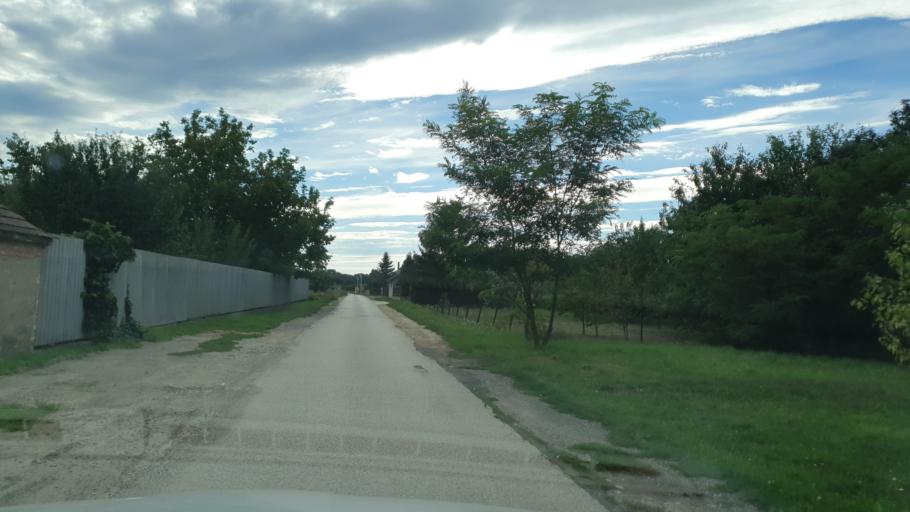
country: HU
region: Heves
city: Zagyvaszanto
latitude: 47.7657
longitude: 19.6694
